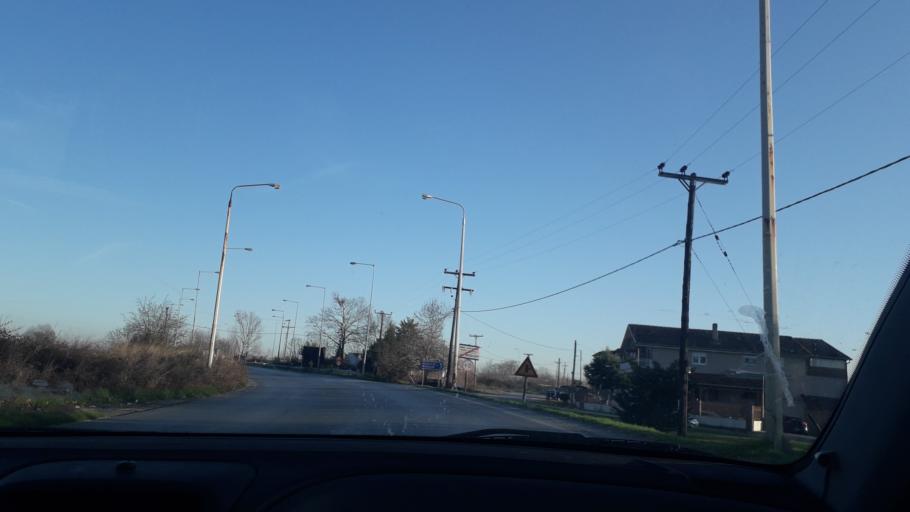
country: GR
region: Central Macedonia
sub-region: Nomos Imathias
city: Agkathia
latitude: 40.5916
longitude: 22.4653
